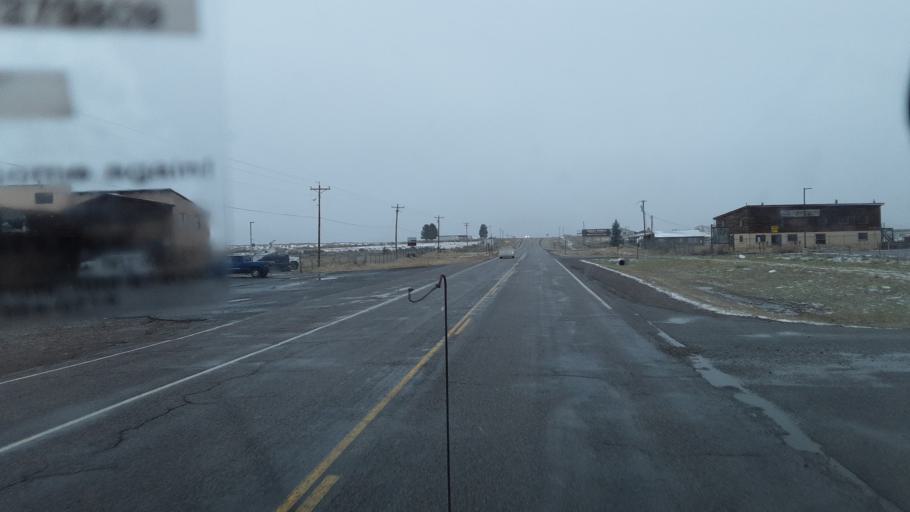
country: US
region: New Mexico
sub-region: Rio Arriba County
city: Tierra Amarilla
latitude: 36.7117
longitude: -106.5596
